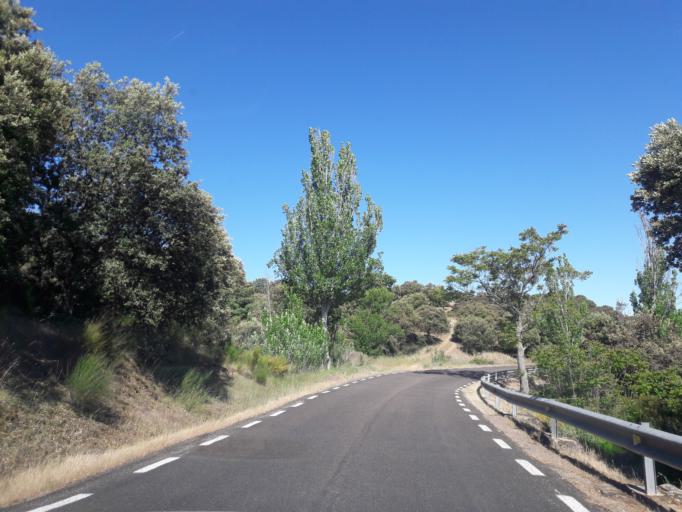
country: ES
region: Castille and Leon
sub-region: Provincia de Salamanca
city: Juzbado
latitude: 41.0697
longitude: -5.9007
